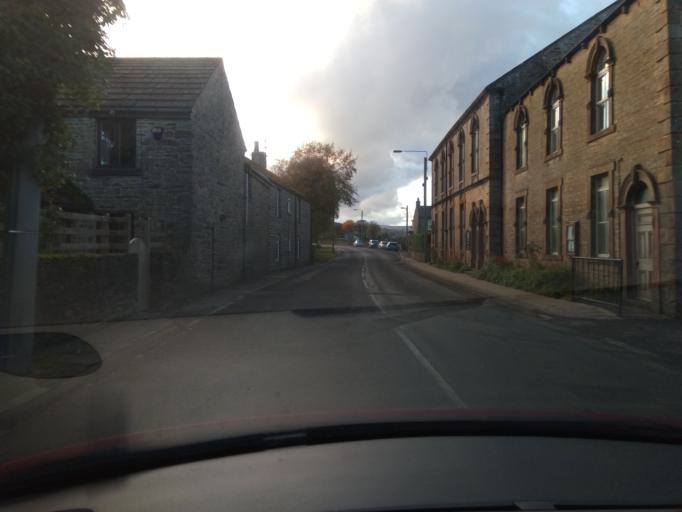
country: GB
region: England
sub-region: County Durham
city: Newbiggin
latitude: 54.7371
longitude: -2.1479
